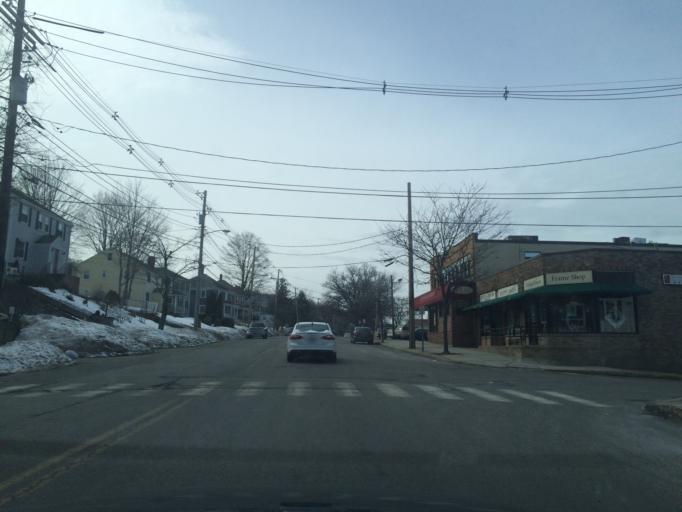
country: US
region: Massachusetts
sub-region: Middlesex County
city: Belmont
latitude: 42.4257
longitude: -71.1945
